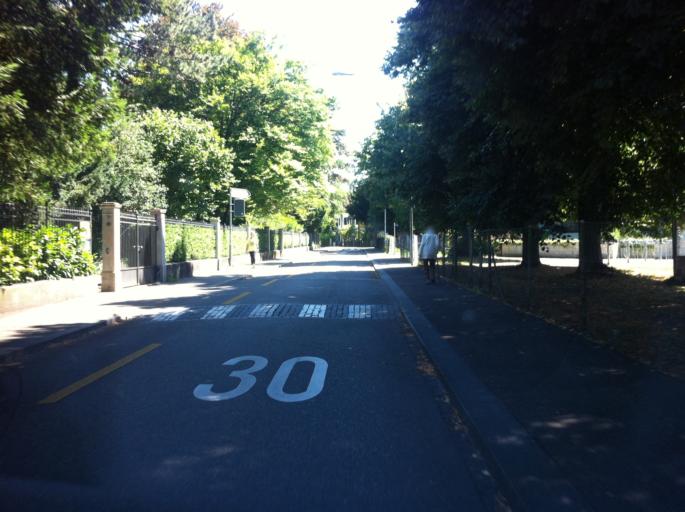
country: CH
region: Zurich
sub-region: Bezirk Zuerich
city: Zuerich (Kreis 8) / Muehlebach
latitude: 47.3604
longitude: 8.5553
